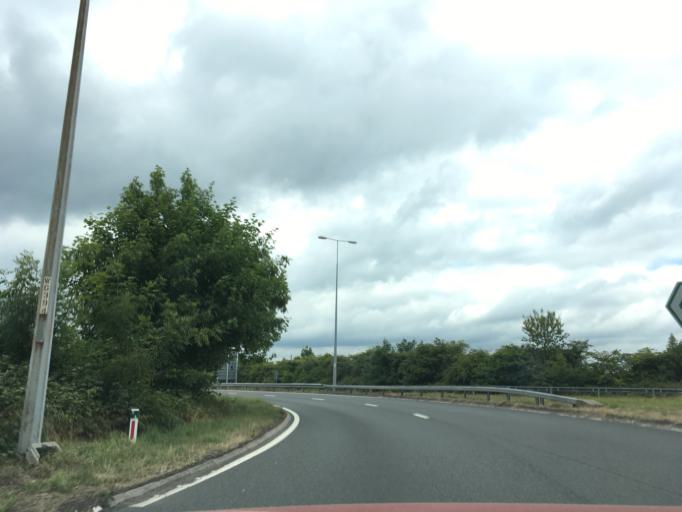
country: GB
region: Wales
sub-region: Torfaen County Borough
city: Cwmbran
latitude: 51.6678
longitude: -3.0058
